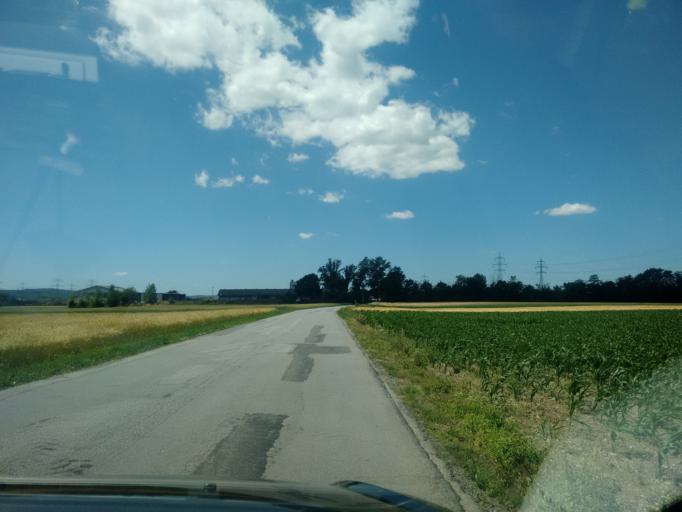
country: AT
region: Lower Austria
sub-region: Politischer Bezirk Tulln
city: Atzenbrugg
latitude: 48.3305
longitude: 15.9128
